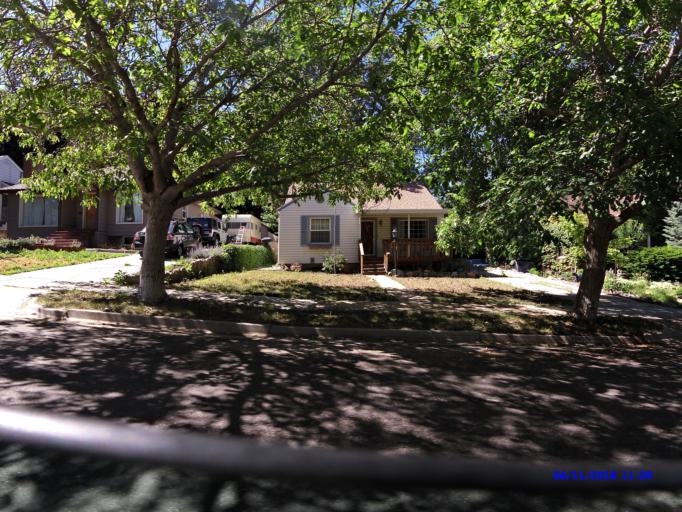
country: US
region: Utah
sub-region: Weber County
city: Ogden
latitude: 41.2192
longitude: -111.9389
